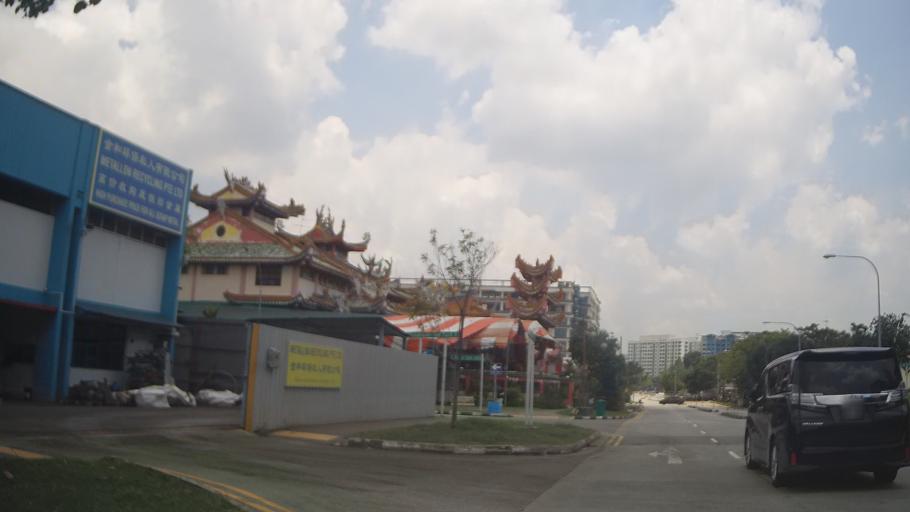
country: MY
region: Johor
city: Johor Bahru
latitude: 1.4519
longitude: 103.7952
